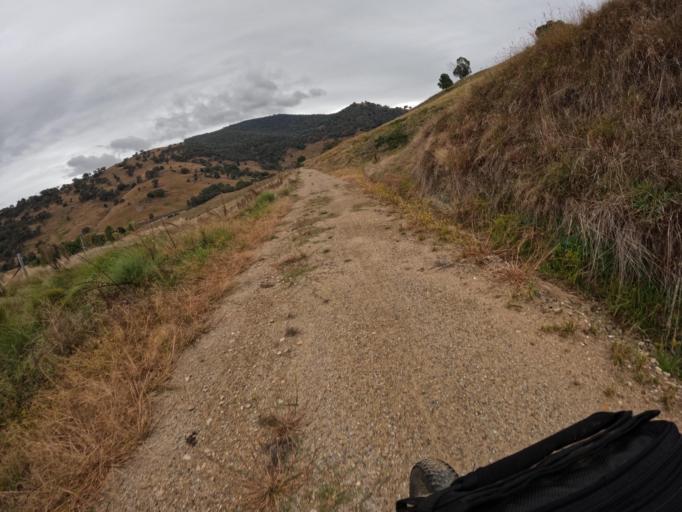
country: AU
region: New South Wales
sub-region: Albury Municipality
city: East Albury
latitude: -36.1841
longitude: 147.3675
